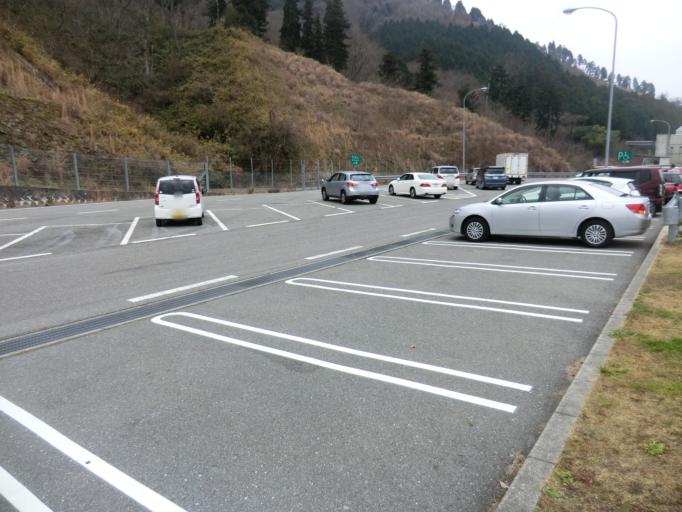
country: JP
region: Hyogo
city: Nishiwaki
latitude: 35.2123
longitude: 134.7939
